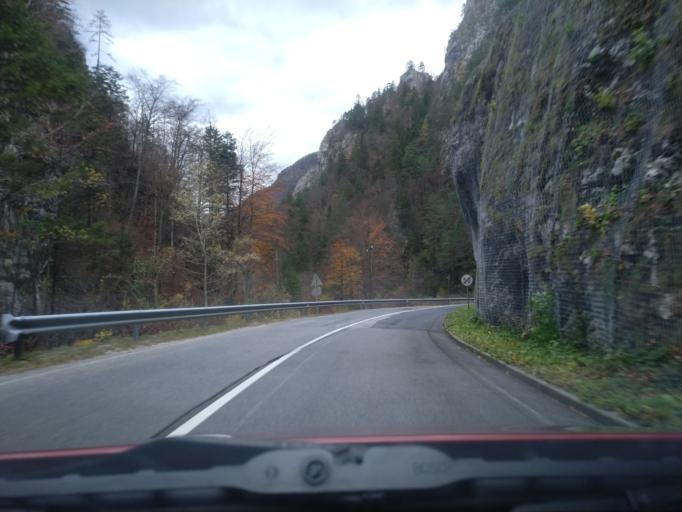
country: SI
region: Luce
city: Luce
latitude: 46.3806
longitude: 14.7272
